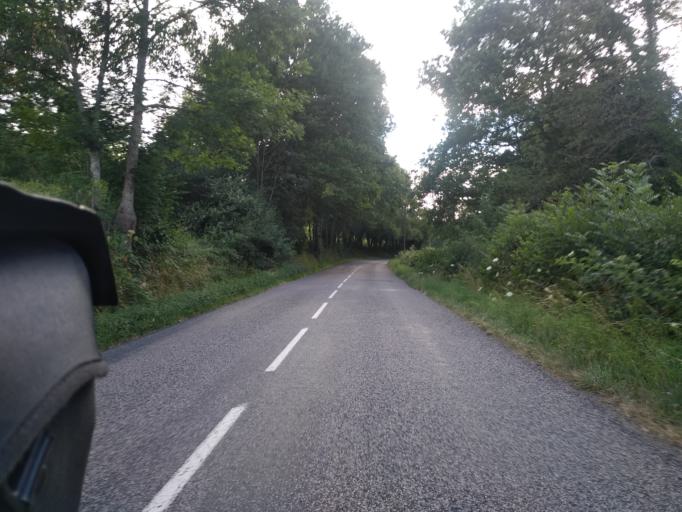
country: FR
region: Rhone-Alpes
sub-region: Departement du Rhone
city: Montrottier
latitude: 45.7887
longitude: 4.5018
